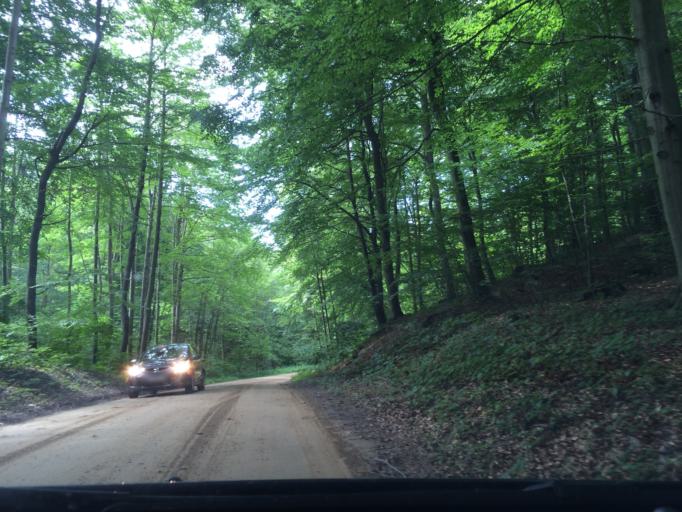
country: DK
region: Zealand
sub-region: Vordingborg Kommune
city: Stege
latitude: 54.9623
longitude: 12.5418
